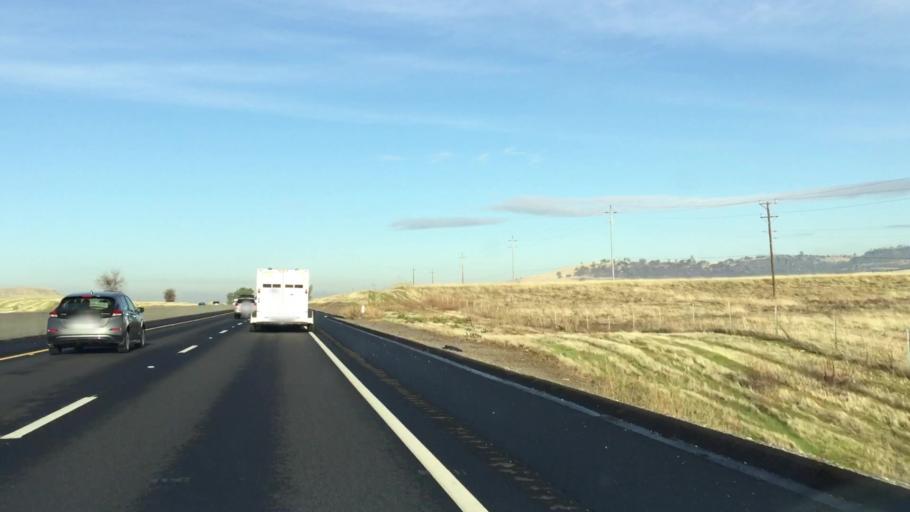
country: US
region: California
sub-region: Butte County
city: Thermalito
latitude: 39.5511
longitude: -121.5965
